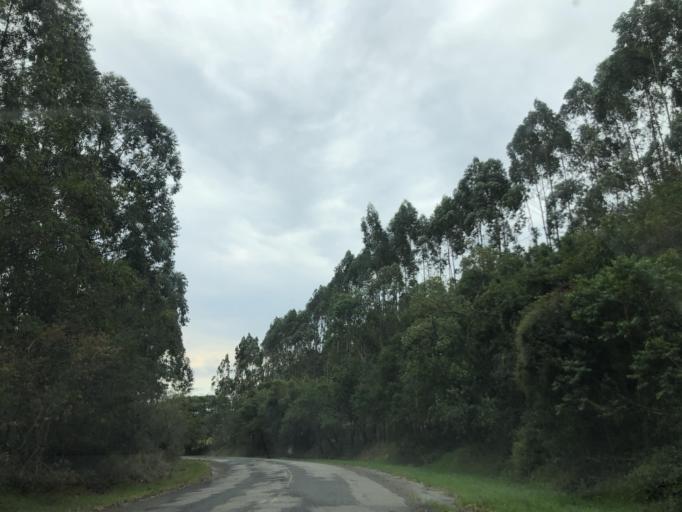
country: BR
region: Sao Paulo
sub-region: Pilar Do Sul
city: Pilar do Sul
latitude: -23.8149
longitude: -47.6330
